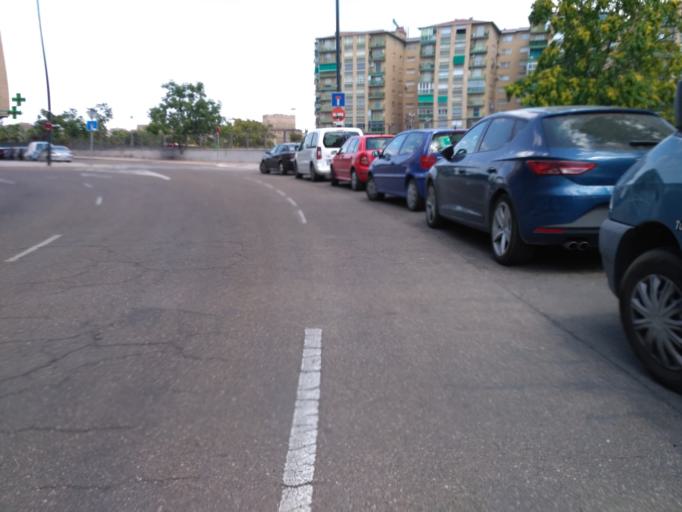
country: ES
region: Aragon
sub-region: Provincia de Zaragoza
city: Almozara
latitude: 41.6537
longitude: -0.8974
